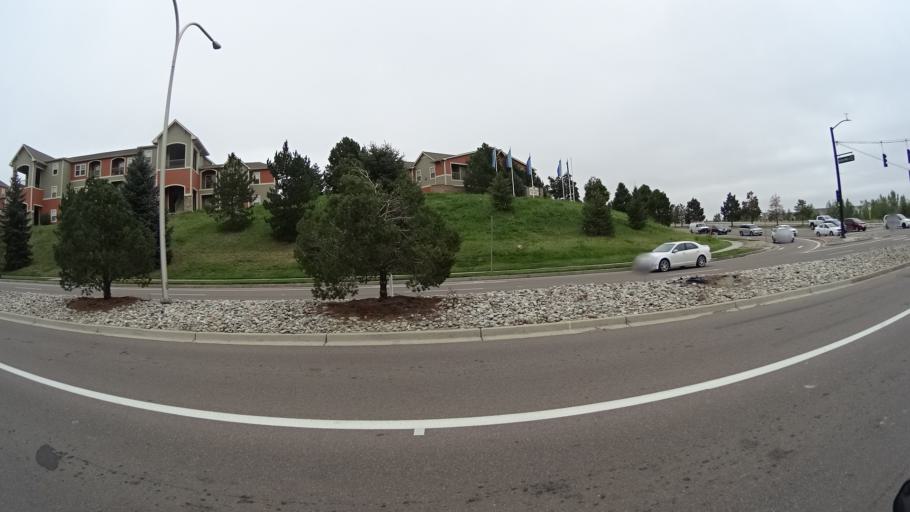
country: US
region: Colorado
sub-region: El Paso County
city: Cimarron Hills
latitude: 38.9108
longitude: -104.7149
